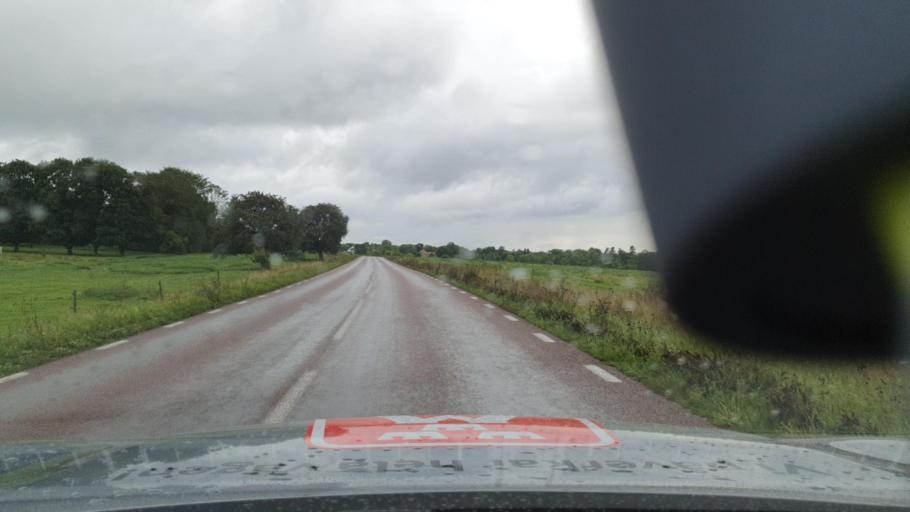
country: SE
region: Gotland
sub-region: Gotland
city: Hemse
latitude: 57.1357
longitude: 18.3454
